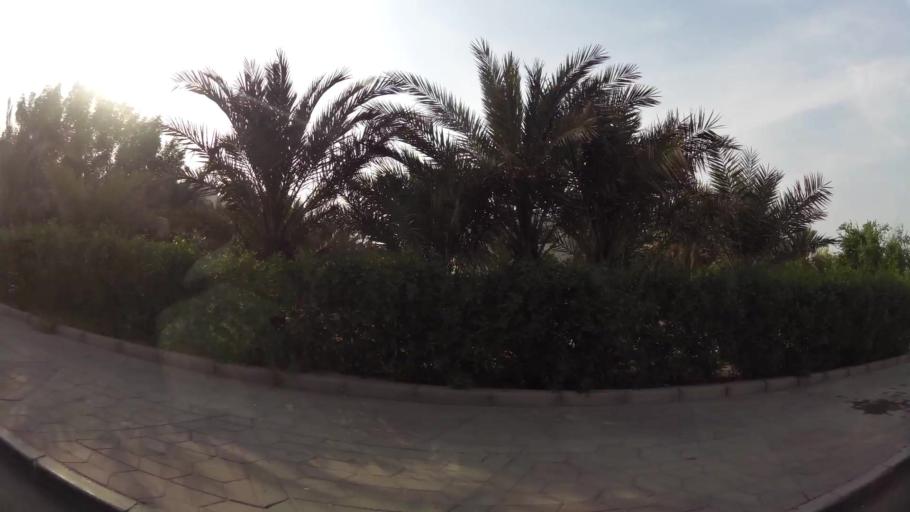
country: KW
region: Mubarak al Kabir
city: Sabah as Salim
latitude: 29.2620
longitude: 48.0566
